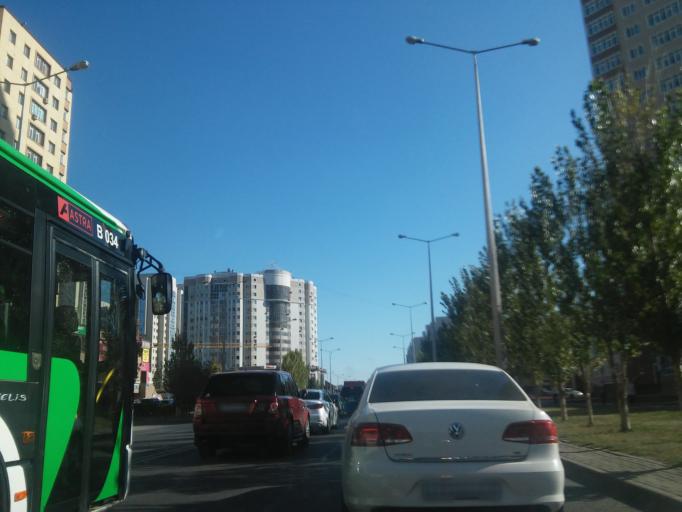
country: KZ
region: Astana Qalasy
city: Astana
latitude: 51.1413
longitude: 71.4757
